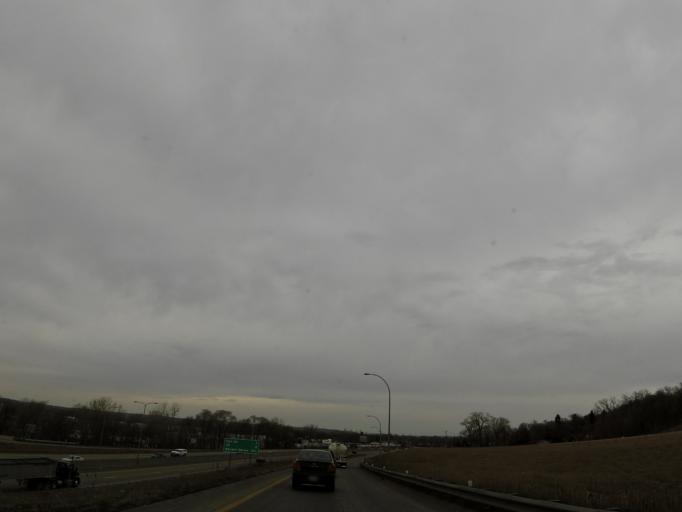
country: US
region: Minnesota
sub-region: Washington County
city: Saint Paul Park
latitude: 44.8520
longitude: -92.9910
